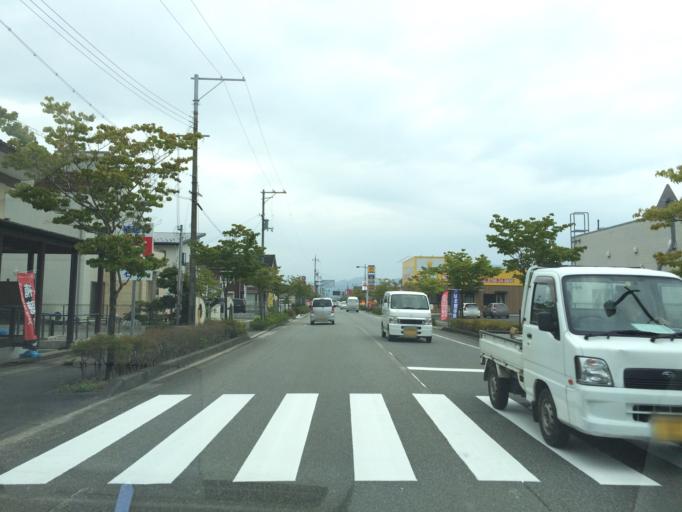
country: JP
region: Hyogo
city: Toyooka
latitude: 35.5331
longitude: 134.8081
